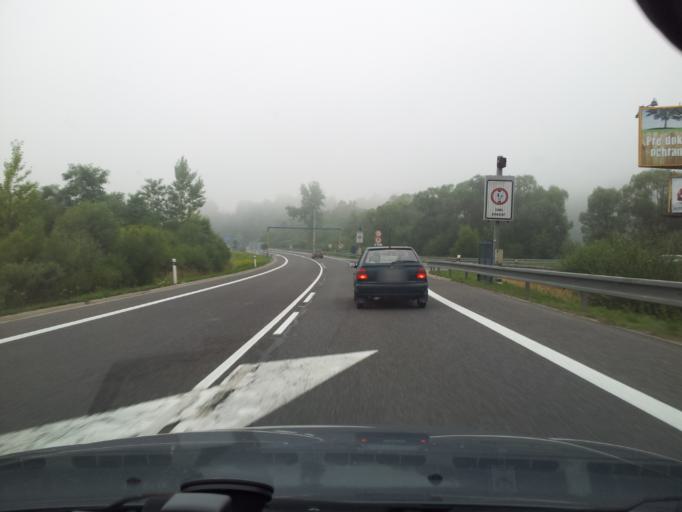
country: SK
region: Zilinsky
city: Cadca
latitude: 49.4212
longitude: 18.8378
